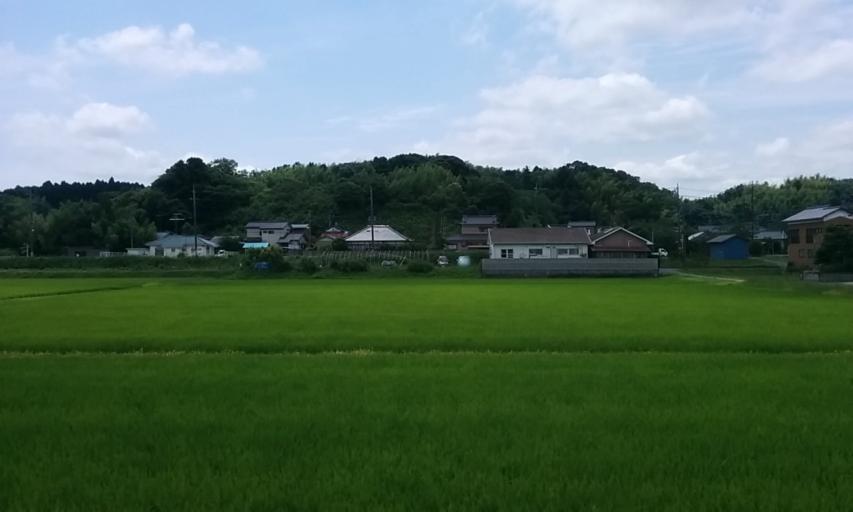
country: JP
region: Ibaraki
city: Edosaki
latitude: 35.8827
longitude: 140.3634
